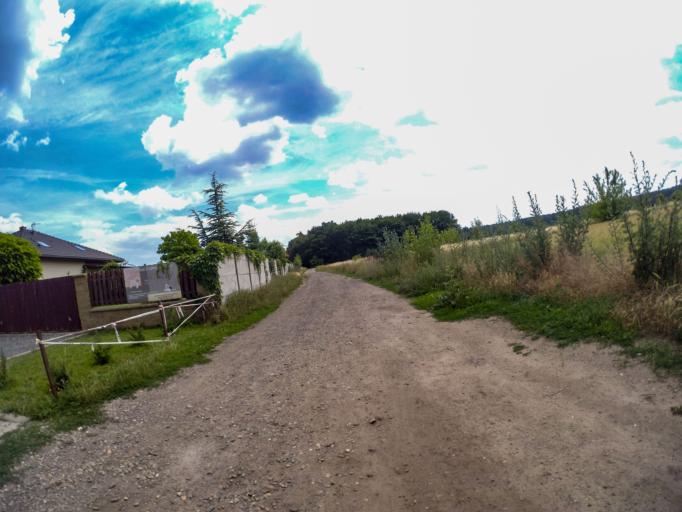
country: CZ
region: Central Bohemia
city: Neratovice
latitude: 50.2511
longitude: 14.5236
